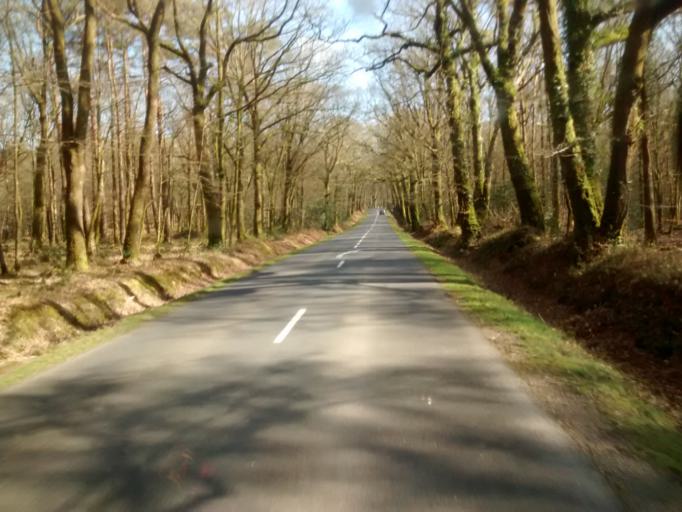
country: FR
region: Brittany
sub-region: Departement d'Ille-et-Vilaine
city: Paimpont
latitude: 48.0159
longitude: -2.1529
